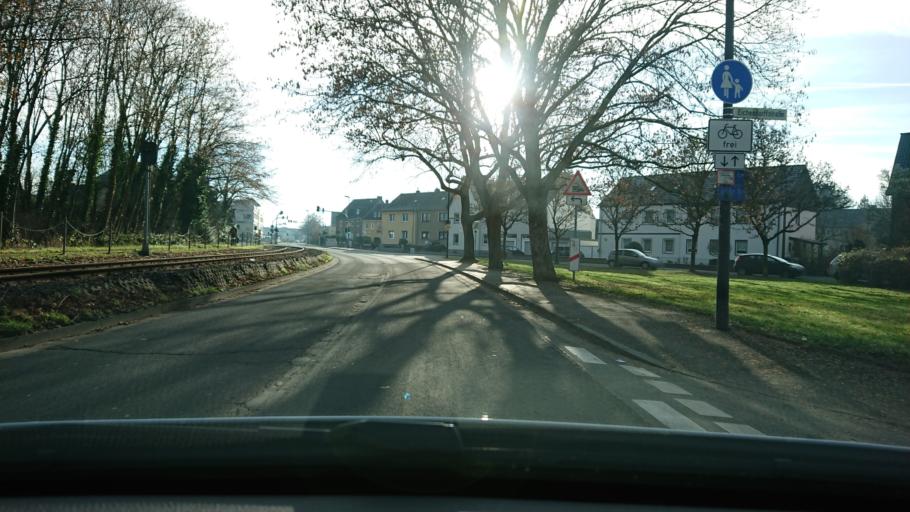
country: DE
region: North Rhine-Westphalia
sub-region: Regierungsbezirk Koln
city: Troisdorf
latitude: 50.8050
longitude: 7.1250
